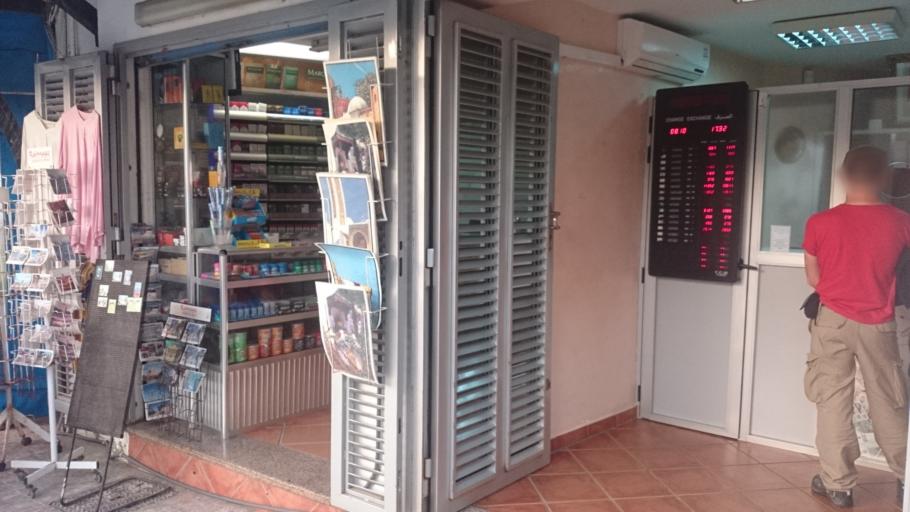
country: MA
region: Tanger-Tetouan
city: Asilah
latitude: 35.4668
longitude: -6.0361
